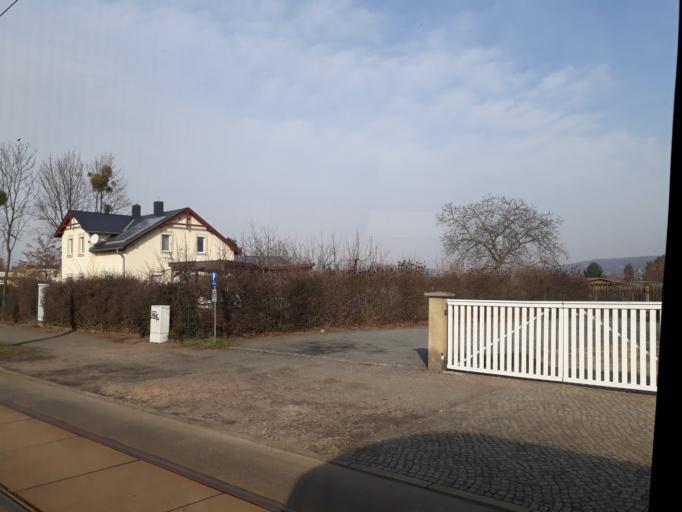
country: DE
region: Saxony
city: Heidenau
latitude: 51.0092
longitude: 13.8368
